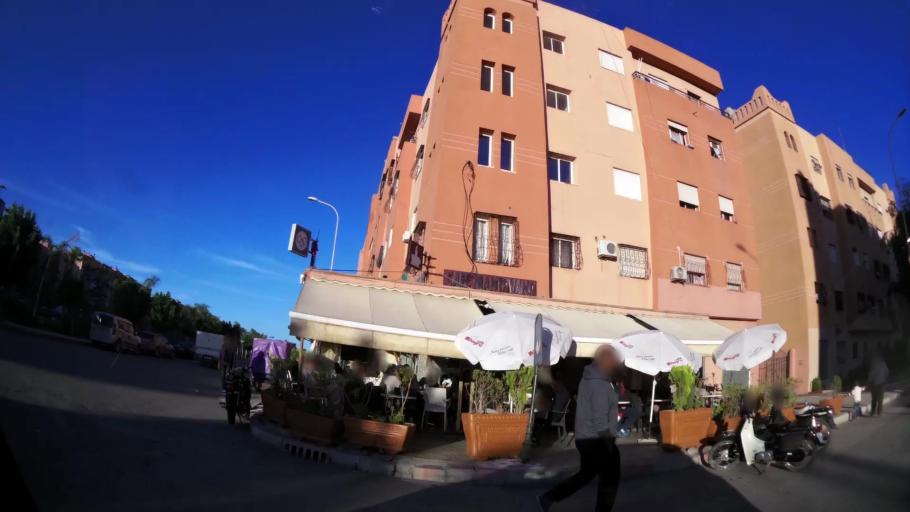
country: MA
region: Marrakech-Tensift-Al Haouz
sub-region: Marrakech
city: Marrakesh
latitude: 31.7503
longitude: -8.1183
